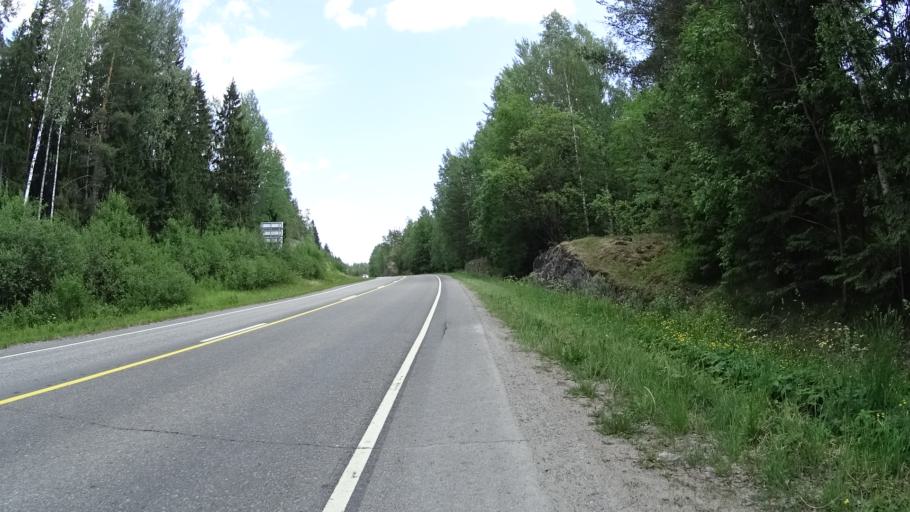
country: FI
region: Uusimaa
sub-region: Raaseporin
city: Pohja
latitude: 60.1034
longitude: 23.5671
